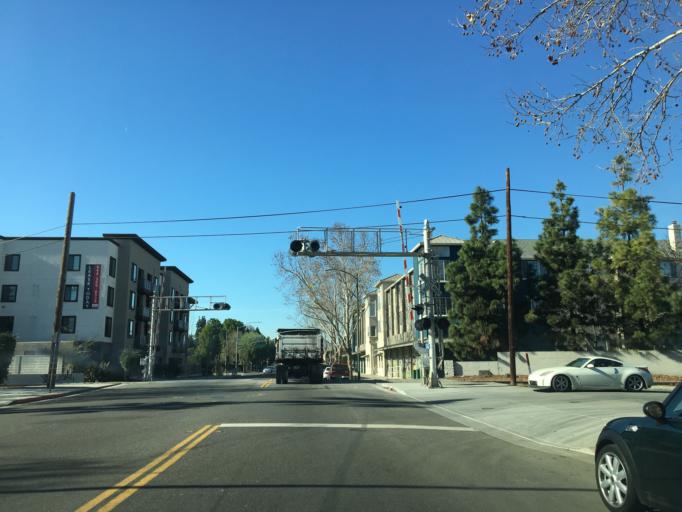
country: US
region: California
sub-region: Santa Clara County
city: San Jose
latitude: 37.3528
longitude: -121.8925
